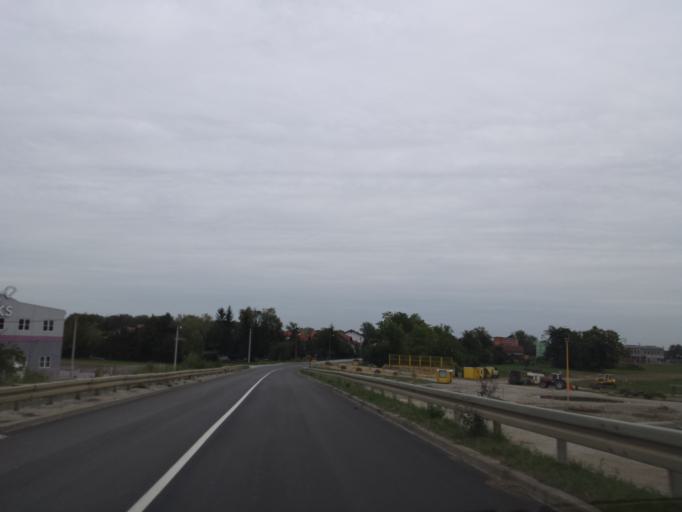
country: HR
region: Grad Zagreb
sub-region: Sesvete
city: Sesvete
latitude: 45.7918
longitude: 16.1294
